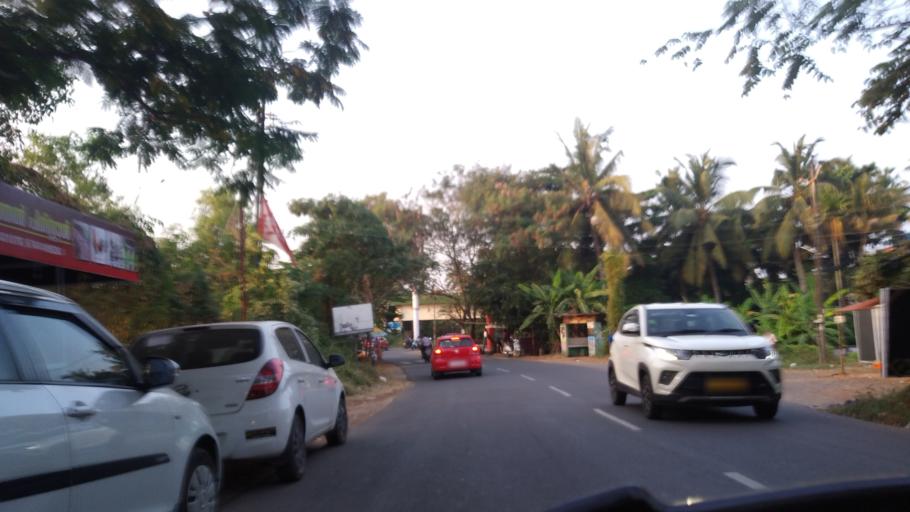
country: IN
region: Kerala
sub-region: Ernakulam
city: Elur
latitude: 10.0484
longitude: 76.2731
